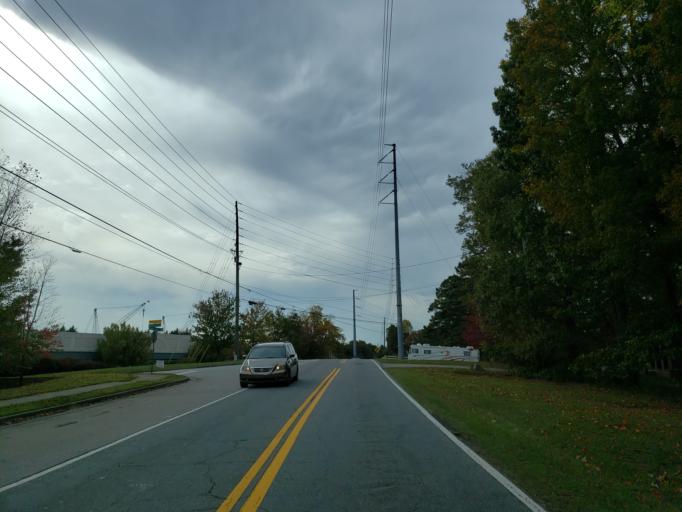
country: US
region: Georgia
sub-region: Cobb County
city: Kennesaw
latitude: 34.0623
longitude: -84.6340
